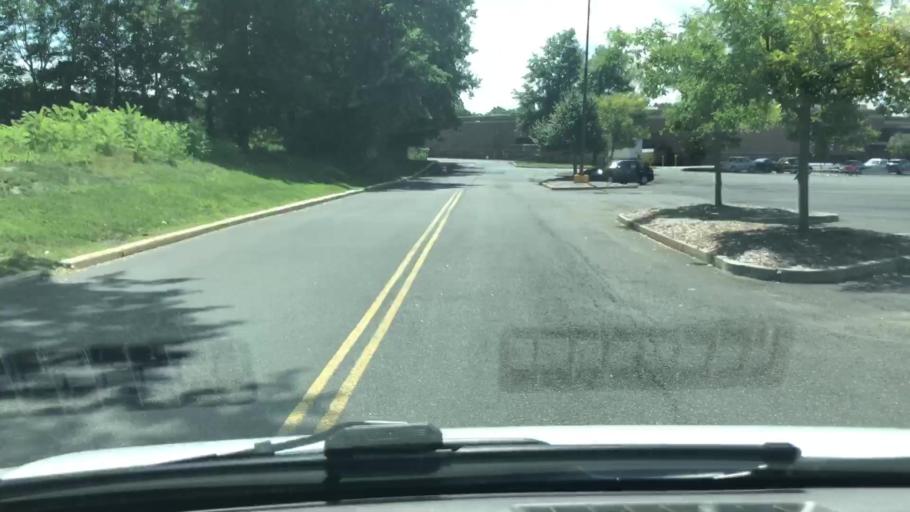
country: US
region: Massachusetts
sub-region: Hampshire County
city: Amherst Center
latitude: 42.3588
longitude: -72.5458
